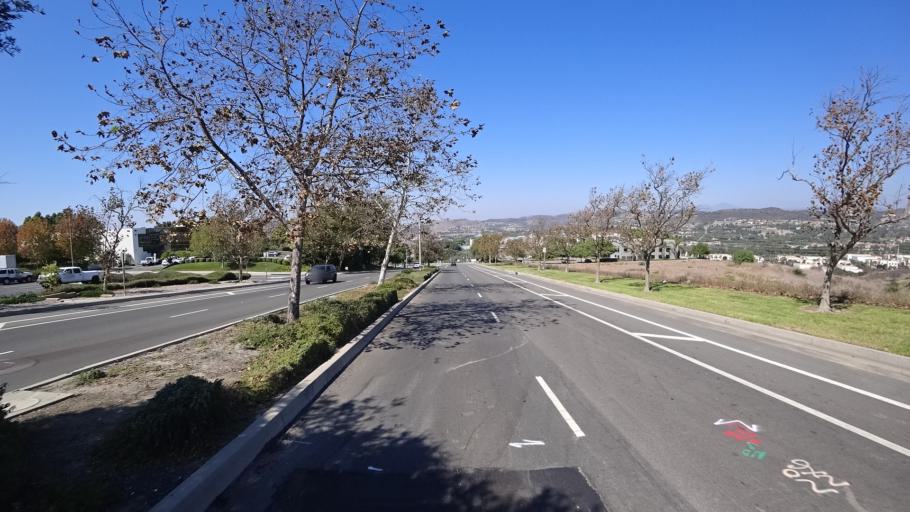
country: US
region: California
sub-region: Orange County
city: San Clemente
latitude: 33.4520
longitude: -117.5929
